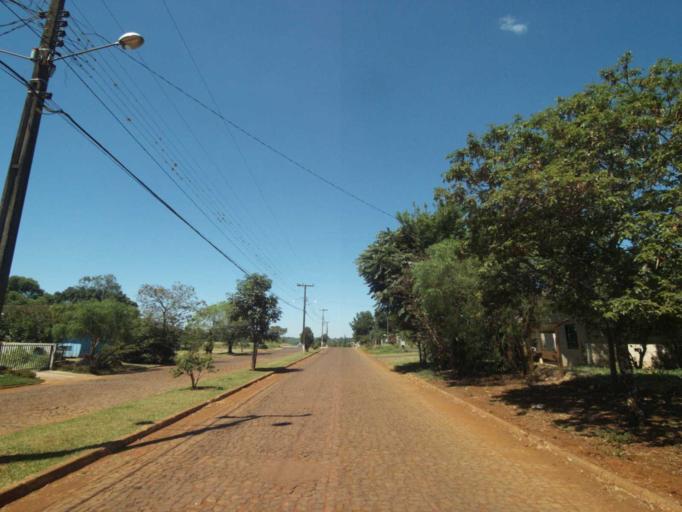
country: BR
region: Parana
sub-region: Laranjeiras Do Sul
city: Laranjeiras do Sul
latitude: -25.3857
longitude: -52.2085
